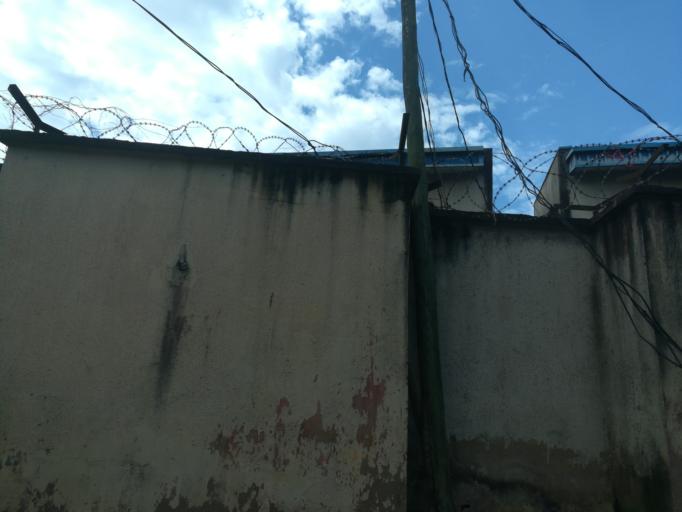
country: NG
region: Lagos
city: Agege
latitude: 6.6036
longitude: 3.3270
